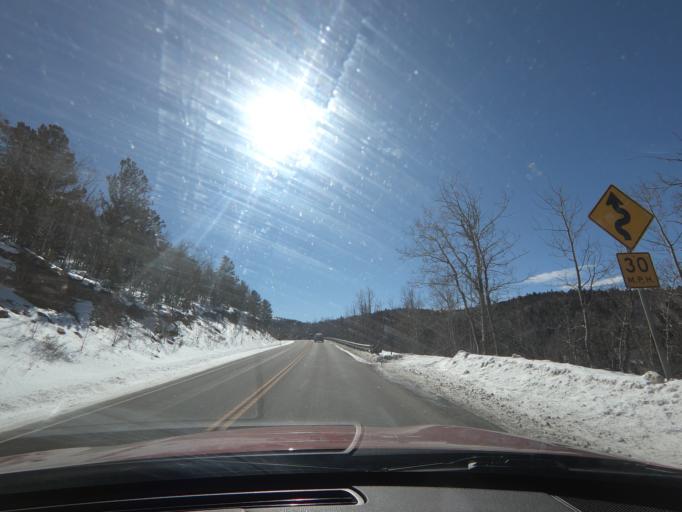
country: US
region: Colorado
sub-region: Teller County
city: Cripple Creek
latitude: 38.8080
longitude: -105.1245
